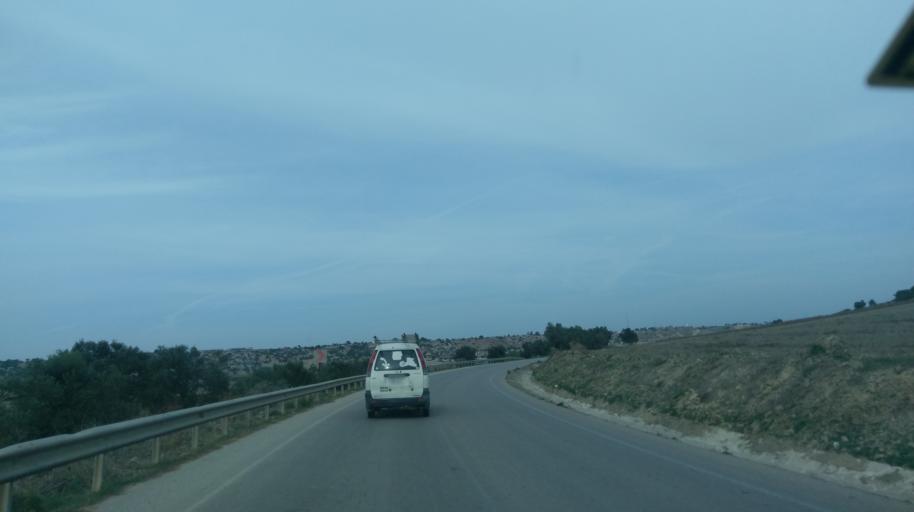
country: CY
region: Ammochostos
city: Leonarisso
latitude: 35.4539
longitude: 34.1274
